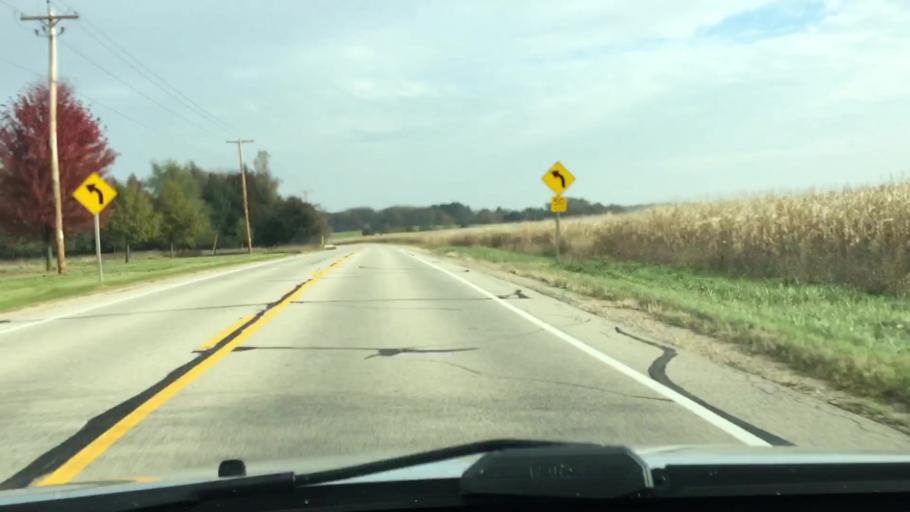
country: US
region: Wisconsin
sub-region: Waukesha County
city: Dousman
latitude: 42.9760
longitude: -88.4687
